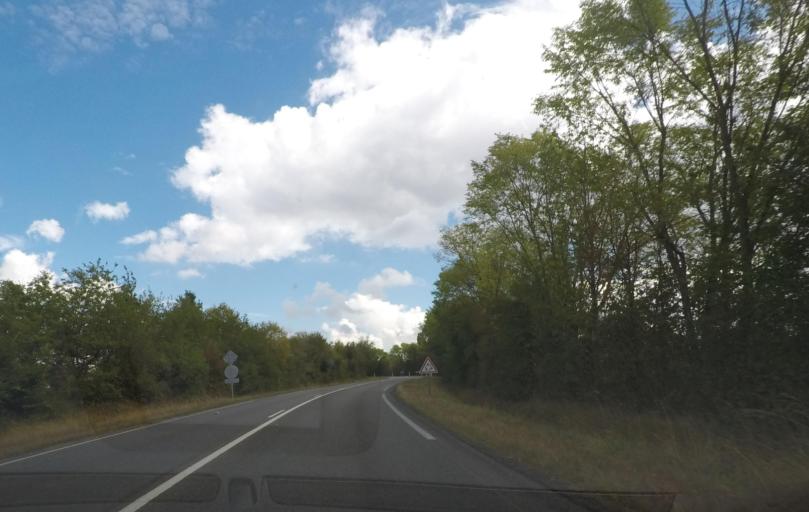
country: FR
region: Pays de la Loire
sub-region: Departement de la Sarthe
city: Champagne
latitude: 48.0796
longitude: 0.3150
